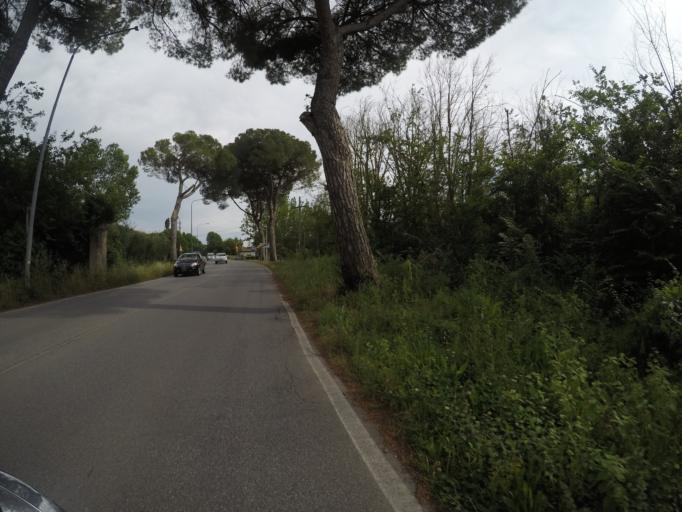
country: IT
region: Tuscany
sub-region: Province of Pisa
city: Madonna dell'Acqua
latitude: 43.7392
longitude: 10.3810
